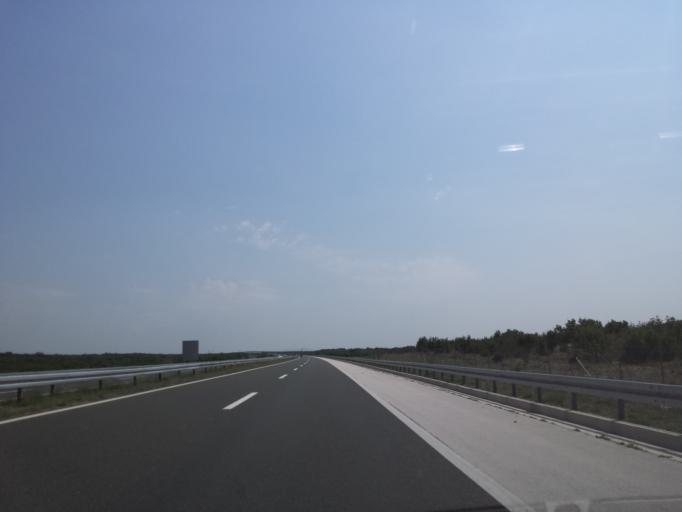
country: HR
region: Sibensko-Kniniska
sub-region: Grad Sibenik
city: Pirovac
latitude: 43.9374
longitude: 15.7052
